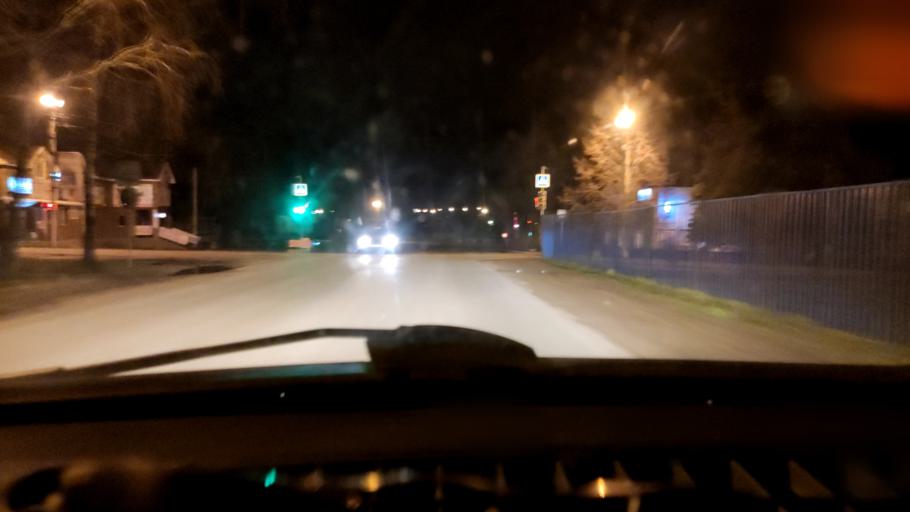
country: RU
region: Bashkortostan
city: Karmaskaly
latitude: 54.3676
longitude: 56.1737
